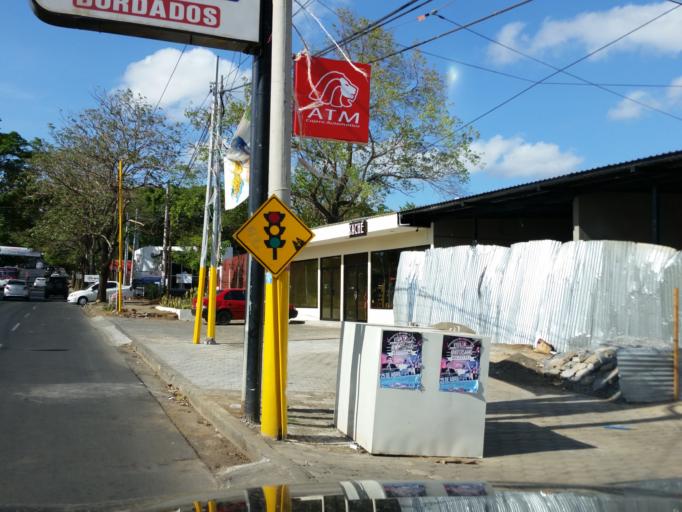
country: NI
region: Managua
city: Managua
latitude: 12.1046
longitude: -86.2629
